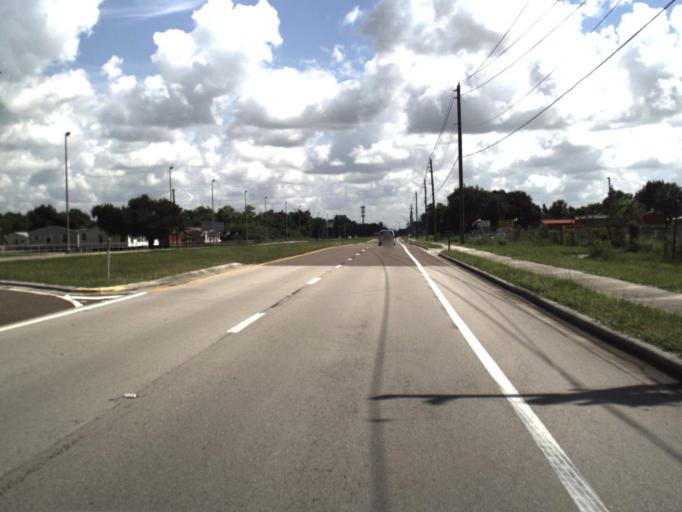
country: US
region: Florida
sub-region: Charlotte County
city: Cleveland
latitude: 26.9669
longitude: -81.9701
